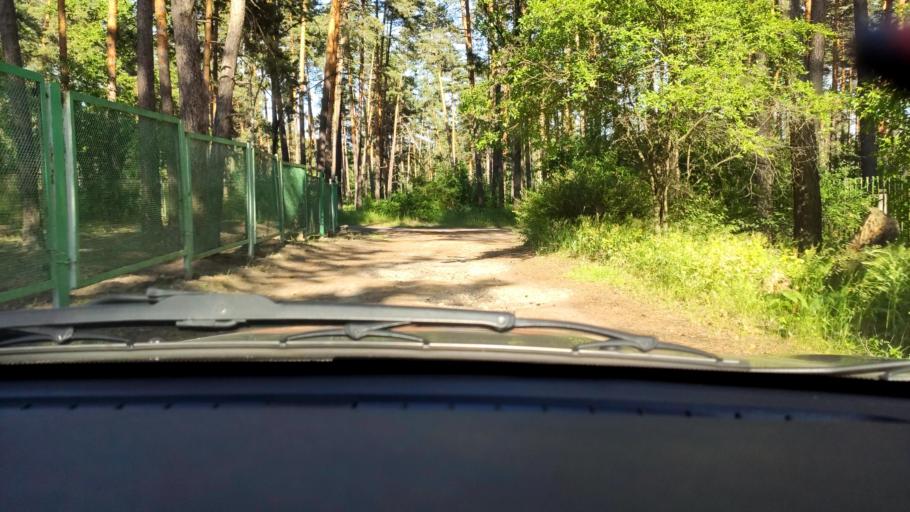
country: RU
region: Voronezj
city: Somovo
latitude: 51.7567
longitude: 39.3741
